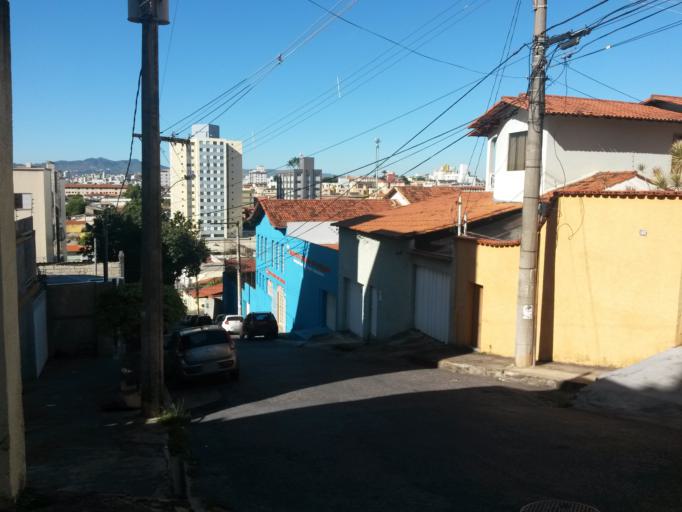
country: BR
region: Minas Gerais
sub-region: Belo Horizonte
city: Belo Horizonte
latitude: -19.9107
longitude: -43.9774
